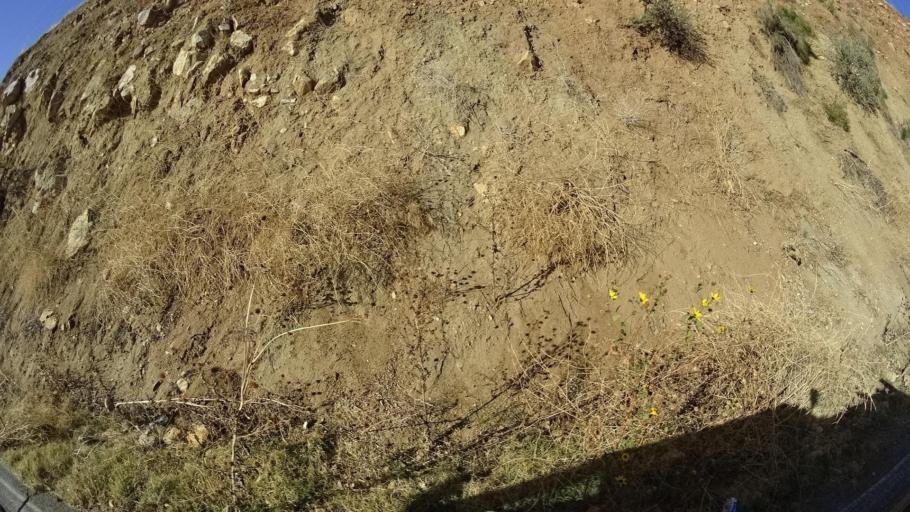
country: US
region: California
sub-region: Kern County
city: Bear Valley Springs
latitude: 35.2936
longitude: -118.6171
